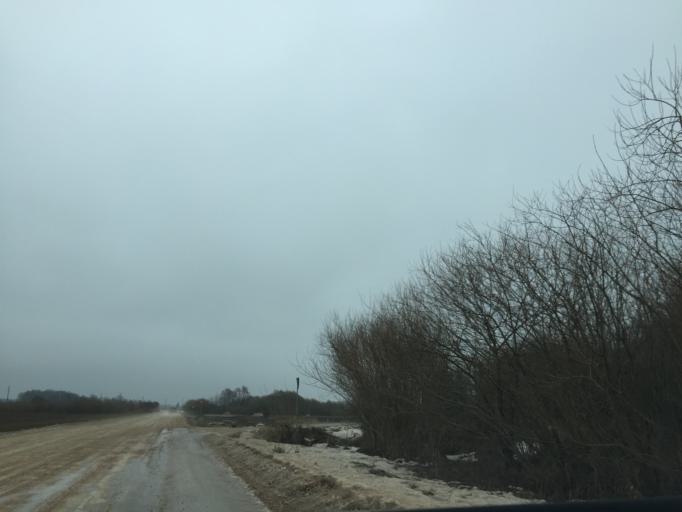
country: LV
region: Ozolnieku
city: Ozolnieki
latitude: 56.6300
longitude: 23.8249
